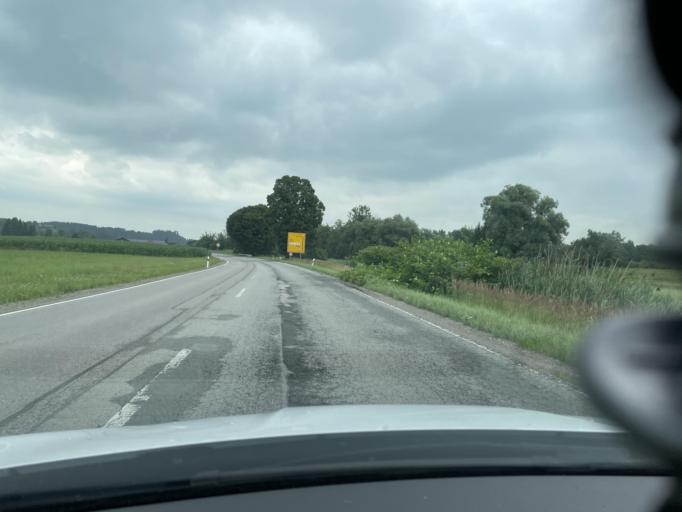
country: DE
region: Bavaria
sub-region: Upper Bavaria
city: Griesstatt
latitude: 47.9860
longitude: 12.1463
